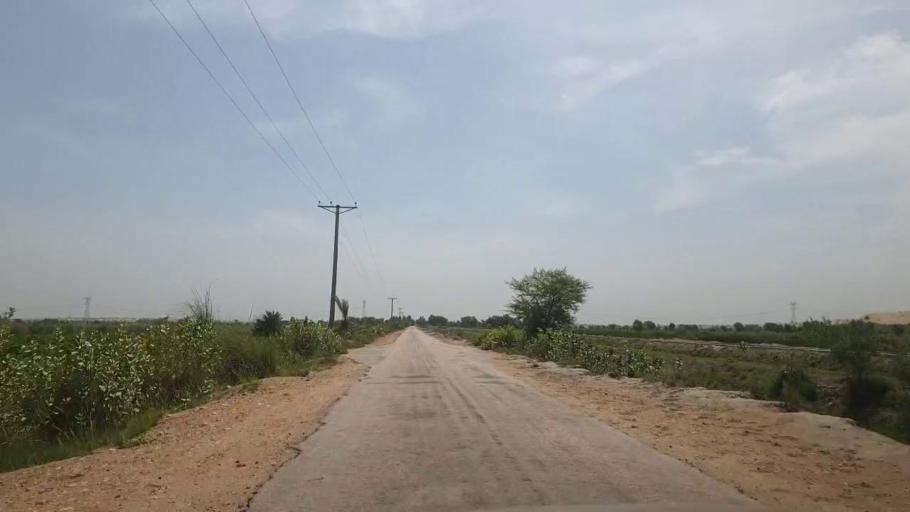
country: PK
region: Sindh
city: Kot Diji
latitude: 27.1091
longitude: 69.0278
